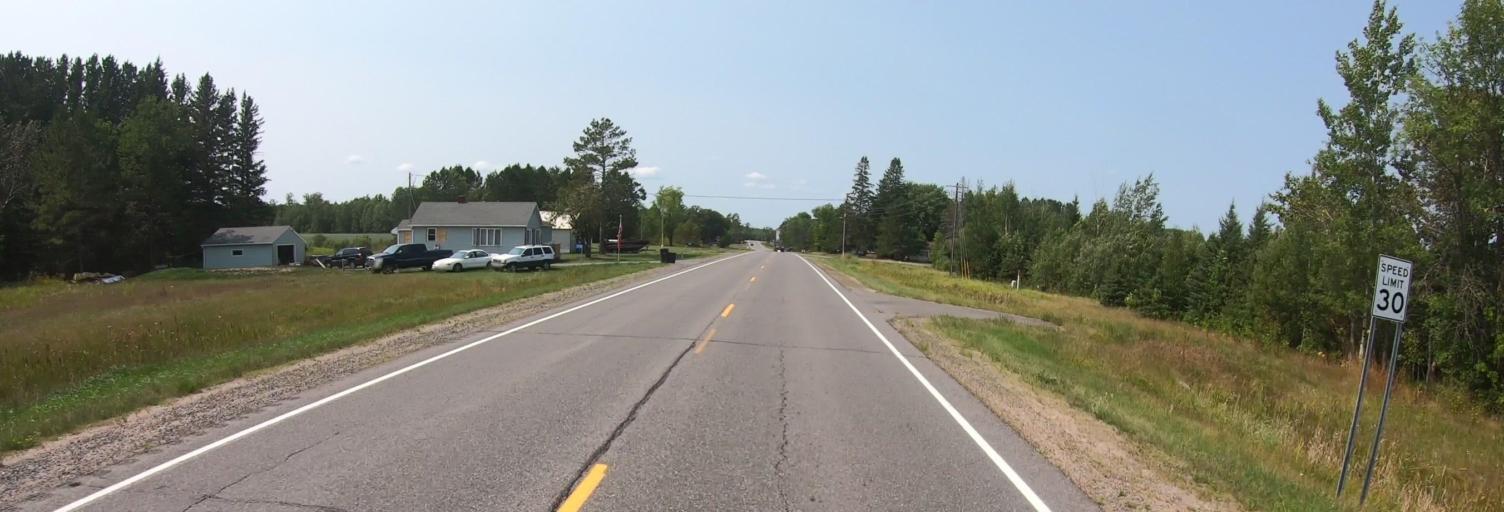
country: US
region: Minnesota
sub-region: Koochiching County
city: International Falls
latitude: 48.5129
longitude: -93.7950
